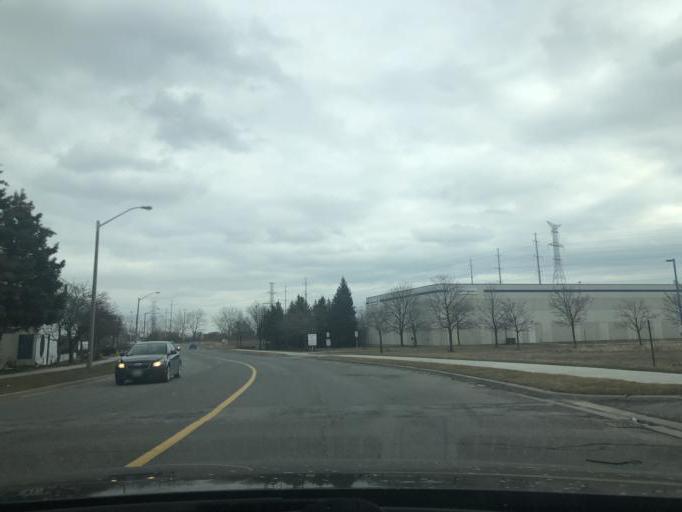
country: CA
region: Ontario
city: Scarborough
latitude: 43.7989
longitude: -79.1952
